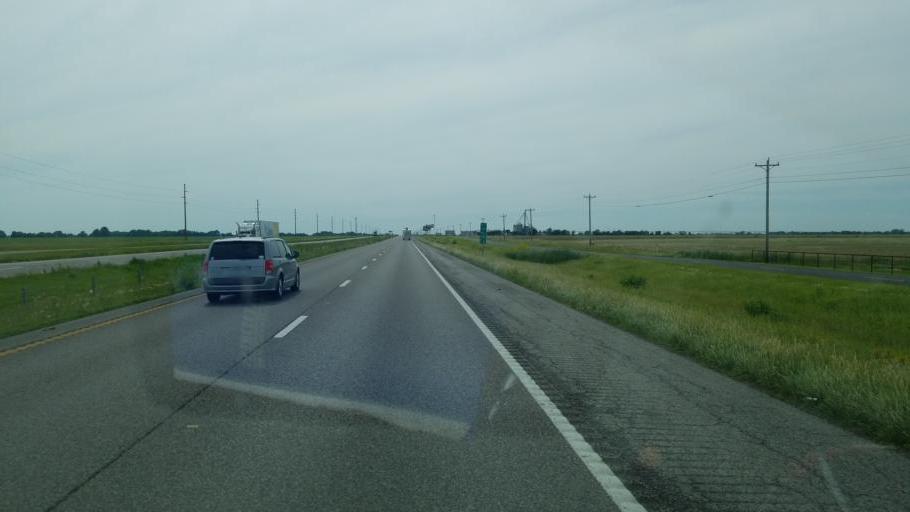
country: US
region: Missouri
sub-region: Callaway County
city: Fulton
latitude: 38.9532
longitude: -92.0617
